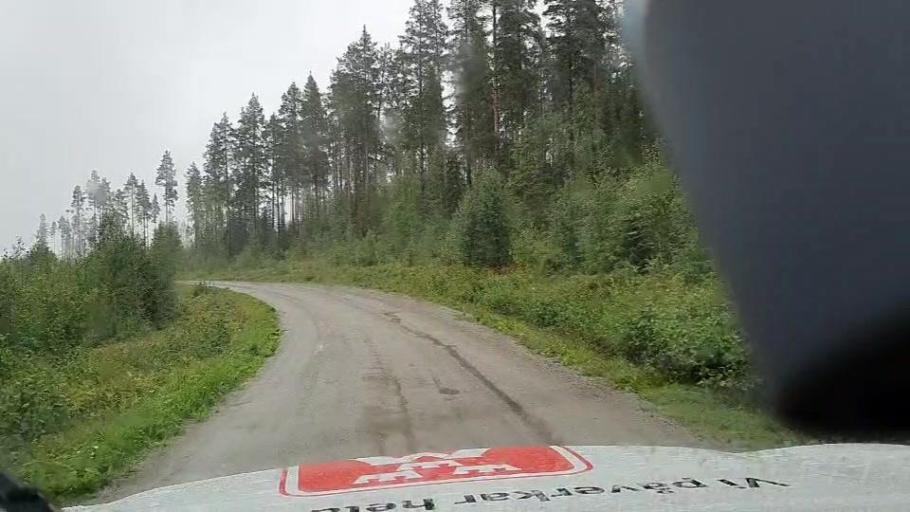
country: SE
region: Jaemtland
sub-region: OEstersunds Kommun
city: Brunflo
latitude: 62.8293
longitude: 15.0243
